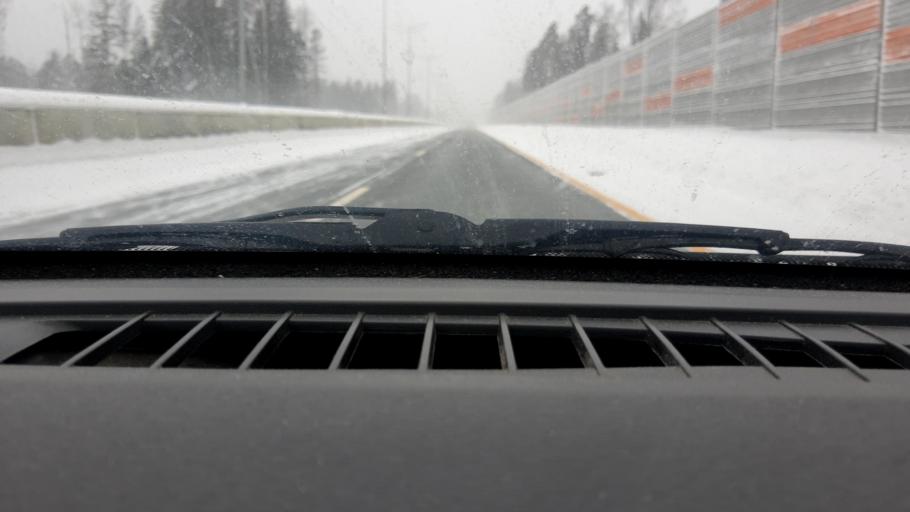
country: RU
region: Moskovskaya
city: Krasnoarmeysk
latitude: 56.0552
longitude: 38.1280
